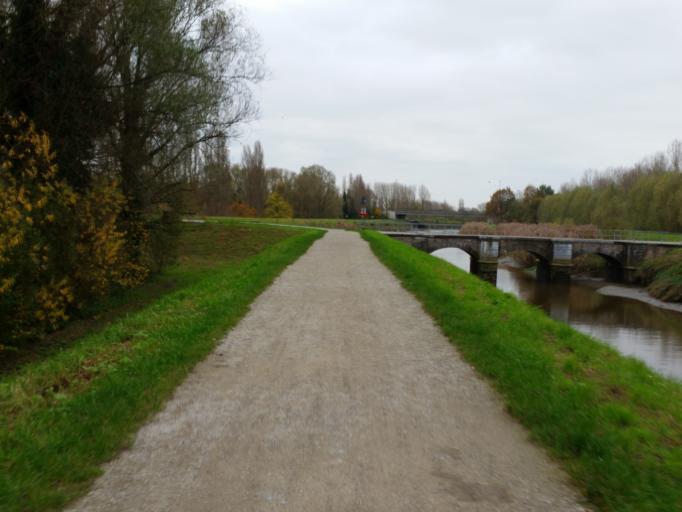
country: BE
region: Flanders
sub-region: Provincie Antwerpen
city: Lier
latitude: 51.1262
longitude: 4.5658
